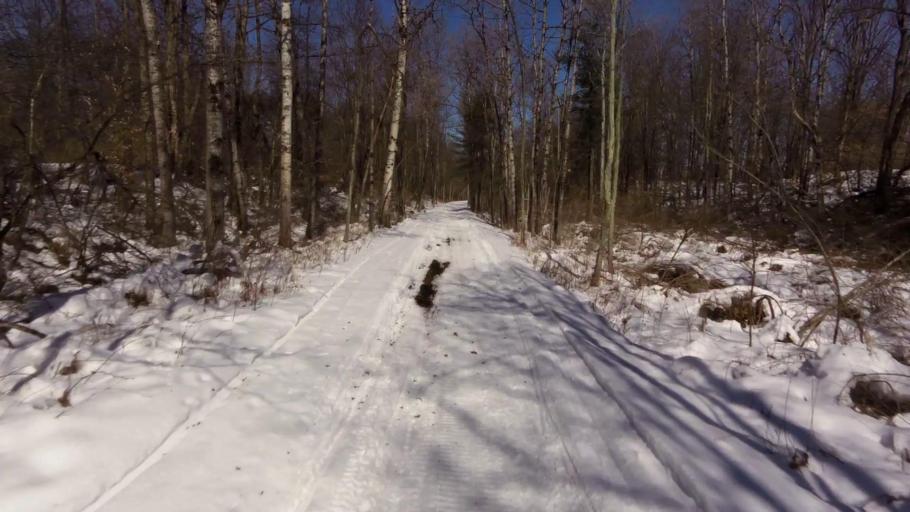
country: US
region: New York
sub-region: Allegany County
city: Houghton
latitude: 42.3624
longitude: -78.1354
